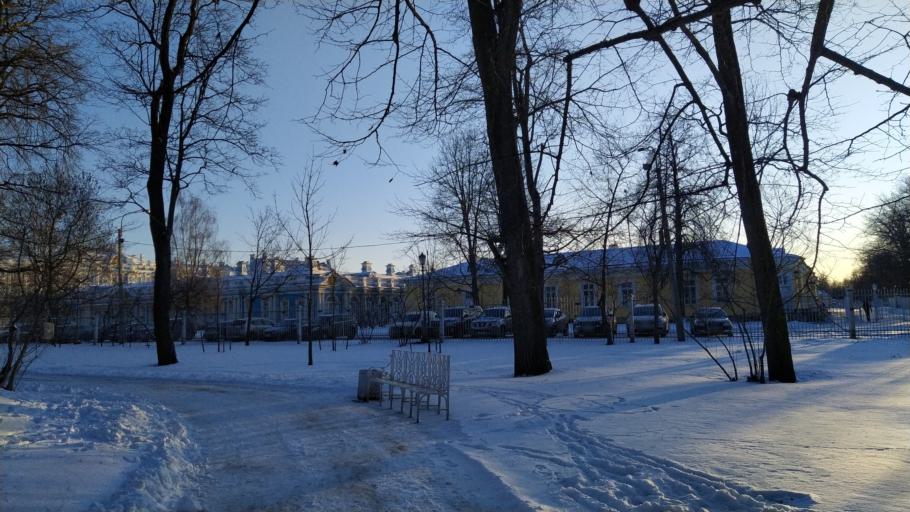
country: RU
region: St.-Petersburg
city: Pushkin
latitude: 59.7184
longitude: 30.3947
